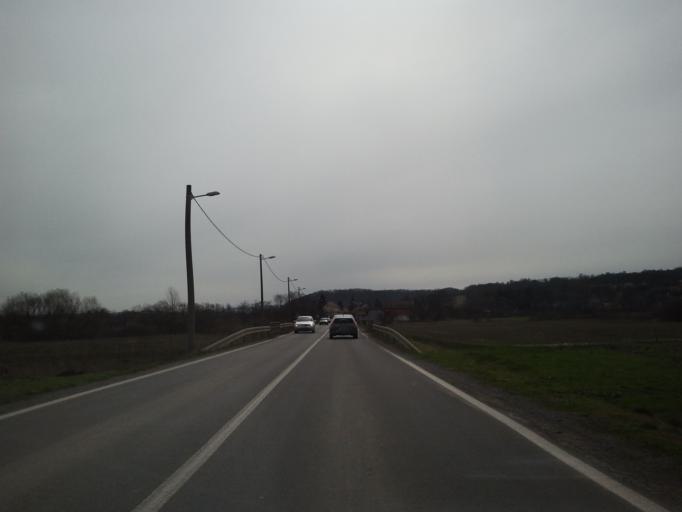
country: HR
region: Sisacko-Moslavacka
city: Glina
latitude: 45.3389
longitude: 16.0780
